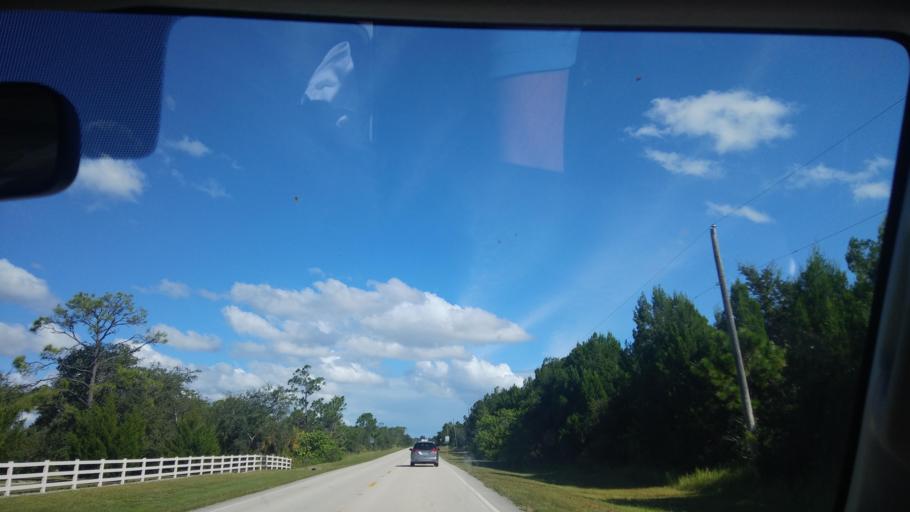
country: US
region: Florida
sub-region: Indian River County
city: Roseland
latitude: 27.8112
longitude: -80.5035
